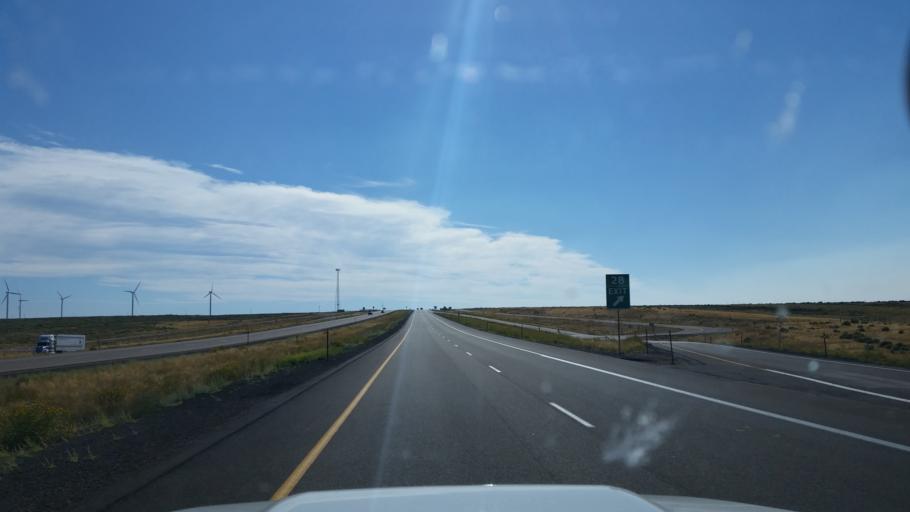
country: US
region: Wyoming
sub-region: Uinta County
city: Mountain View
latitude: 41.3039
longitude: -110.5355
